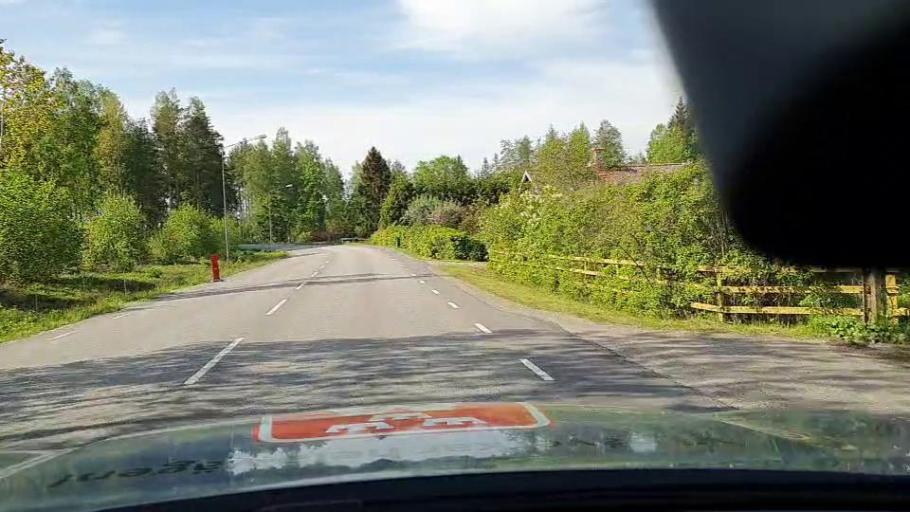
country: SE
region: Soedermanland
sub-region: Eskilstuna Kommun
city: Arla
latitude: 59.2913
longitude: 16.6761
